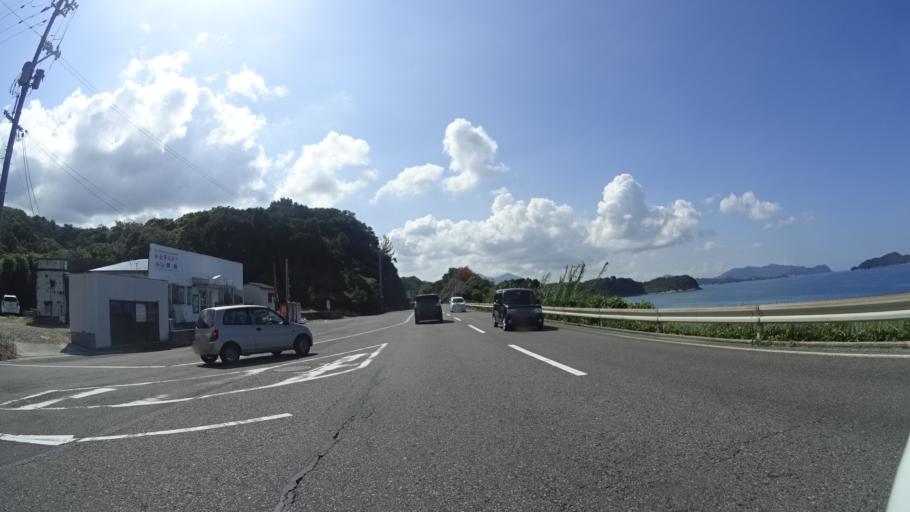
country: JP
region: Yamaguchi
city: Shimonoseki
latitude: 34.1922
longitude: 130.9332
